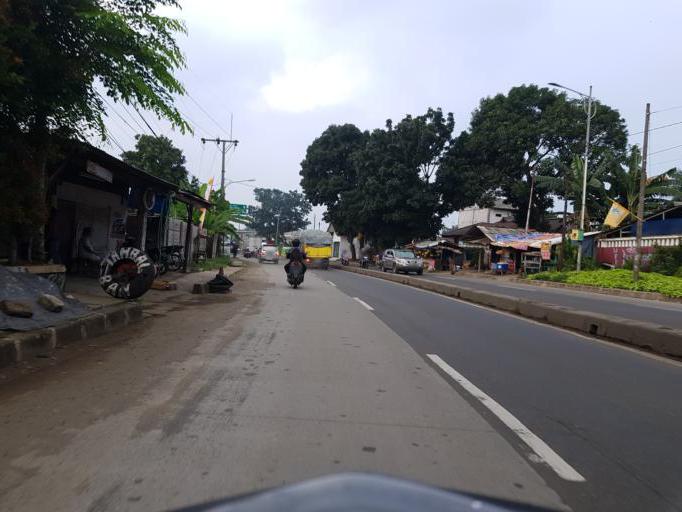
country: ID
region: West Java
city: Ciampea
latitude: -6.5000
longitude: 106.7575
